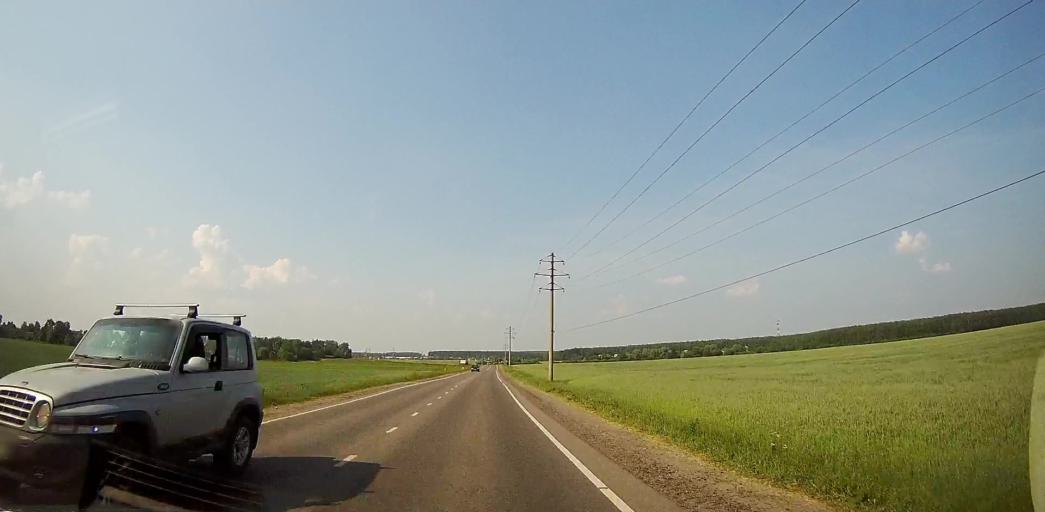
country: RU
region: Moskovskaya
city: Barybino
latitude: 55.2577
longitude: 37.9189
